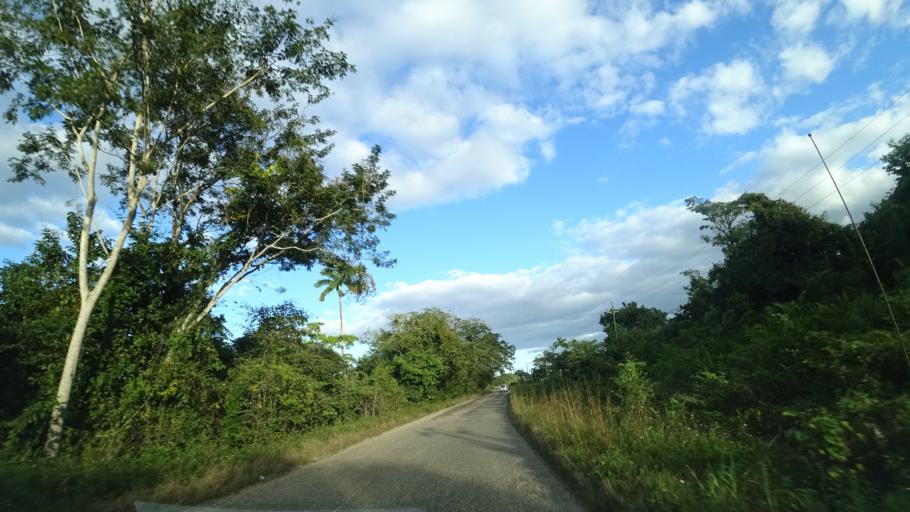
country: BZ
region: Belize
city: Belize City
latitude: 17.5717
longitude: -88.3933
